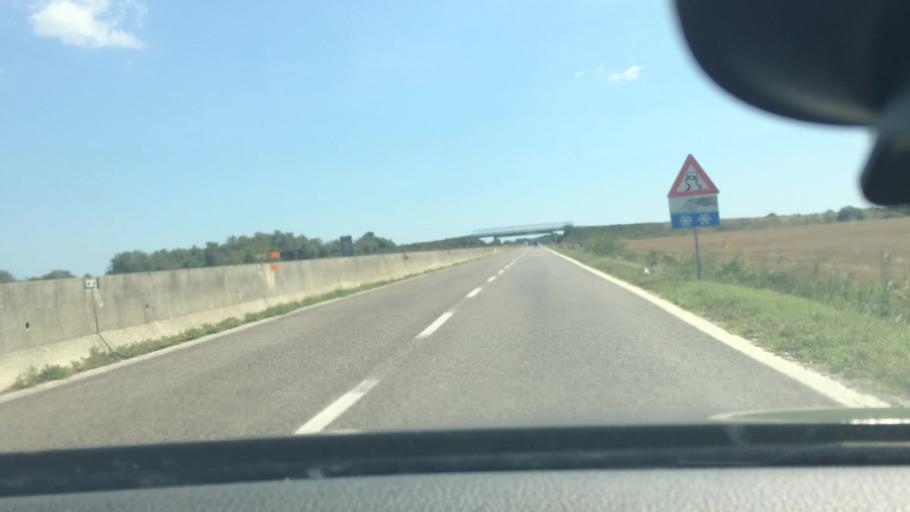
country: IT
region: Emilia-Romagna
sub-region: Provincia di Ferrara
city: Ostellato
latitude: 44.7546
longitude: 11.9789
